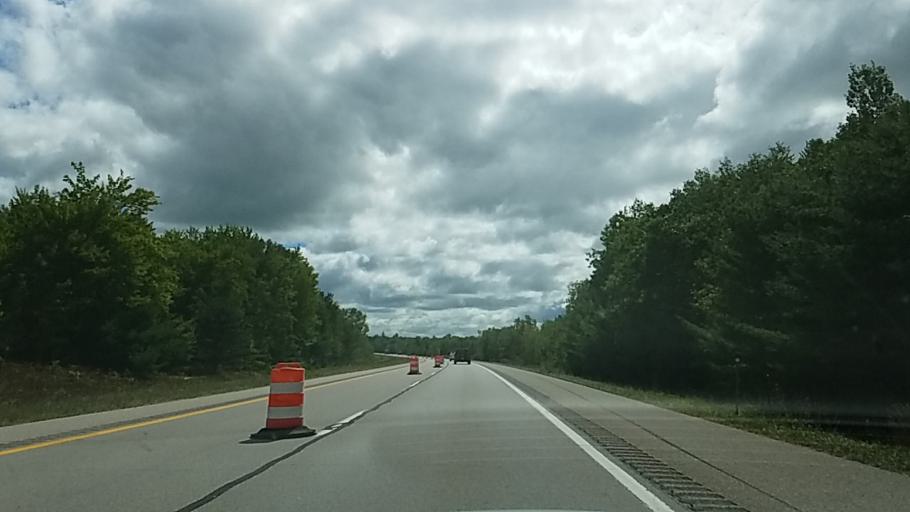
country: US
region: Michigan
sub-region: Arenac County
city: Standish
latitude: 44.0073
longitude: -84.0383
